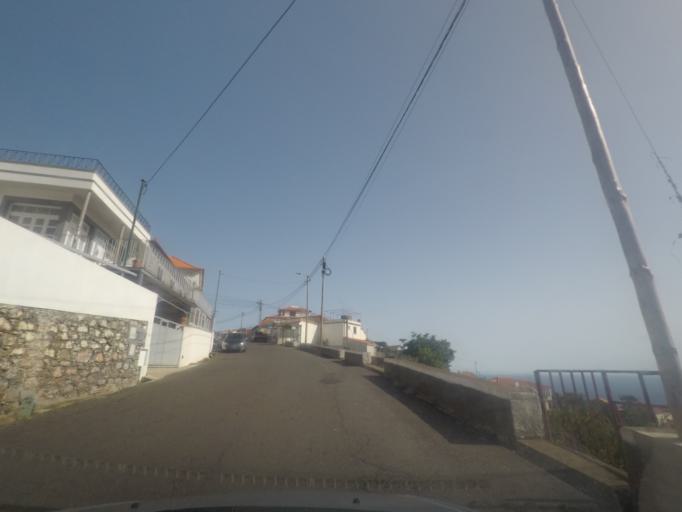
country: PT
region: Madeira
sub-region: Calheta
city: Estreito da Calheta
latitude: 32.7302
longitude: -17.1728
